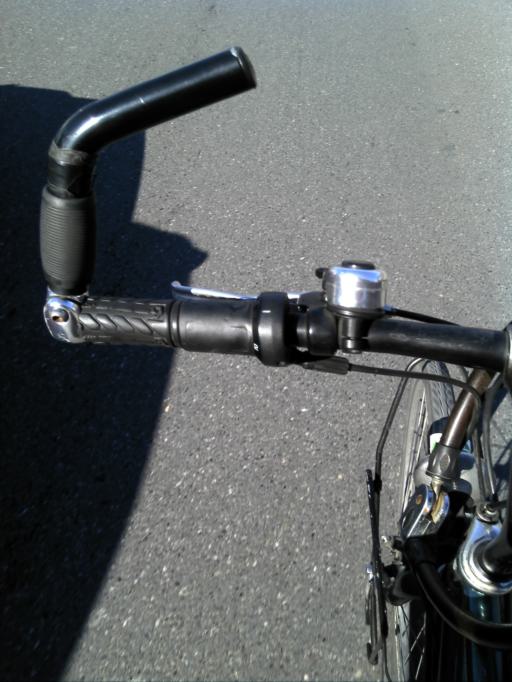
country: AL
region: Shkoder
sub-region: Rrethi i Shkodres
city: Shkoder
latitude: 42.0862
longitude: 19.5088
